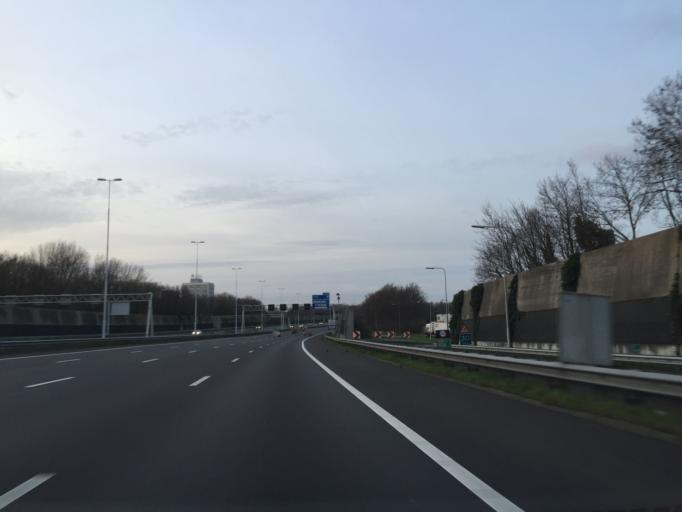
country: NL
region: South Holland
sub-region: Gemeente Zwijndrecht
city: Zwijndrecht
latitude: 51.8139
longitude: 4.6358
